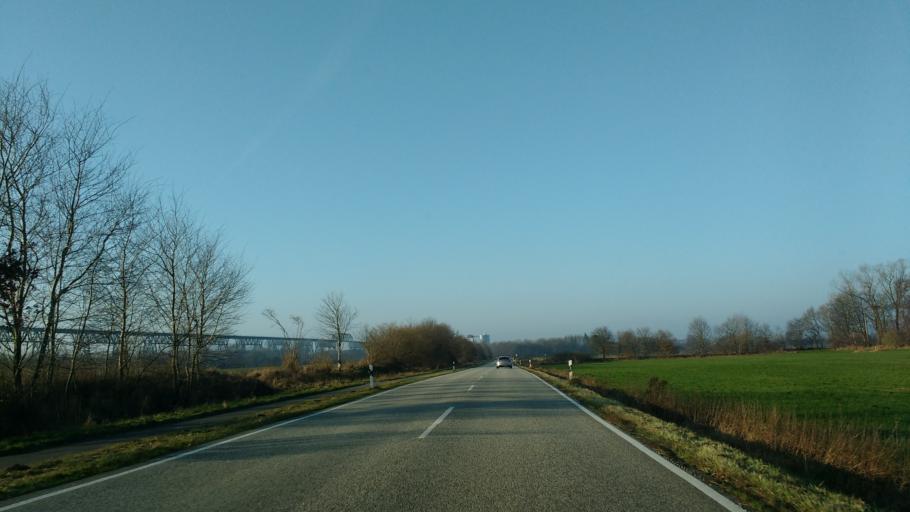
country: DE
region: Schleswig-Holstein
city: Gribbohm
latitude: 54.0179
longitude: 9.3191
